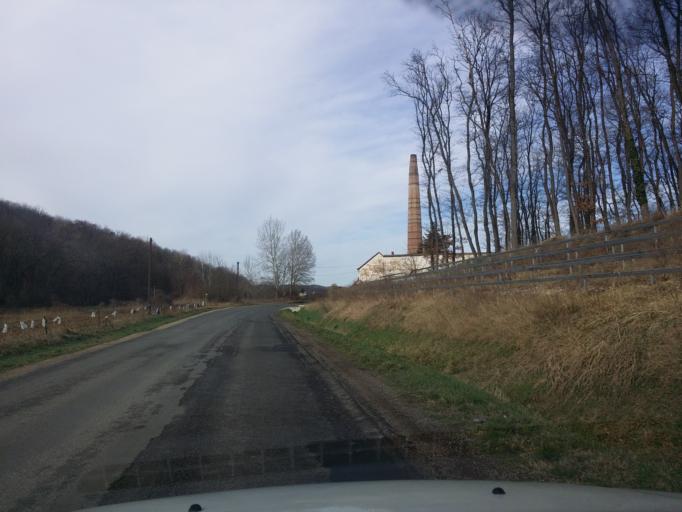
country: HU
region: Baranya
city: Villany
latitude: 45.8780
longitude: 18.4417
